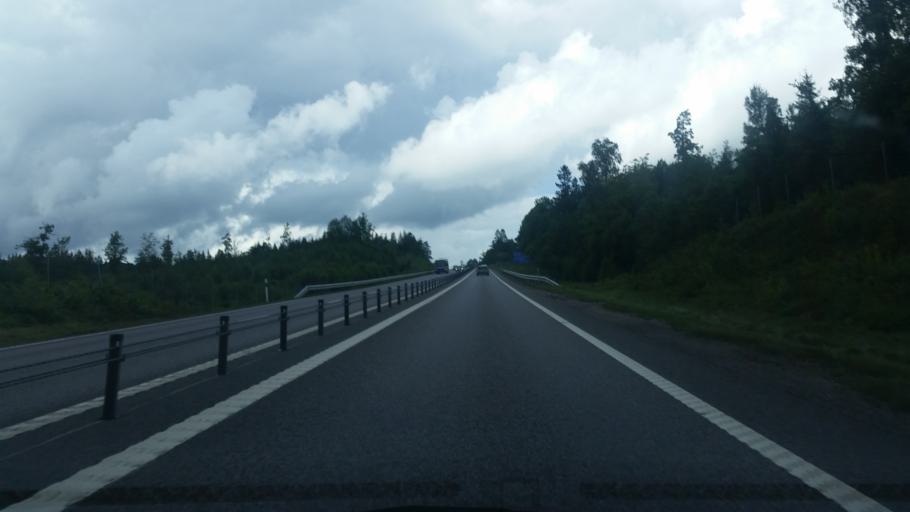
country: SE
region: Vaestra Goetaland
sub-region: Boras Kommun
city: Dalsjofors
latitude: 57.6426
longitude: 13.0705
